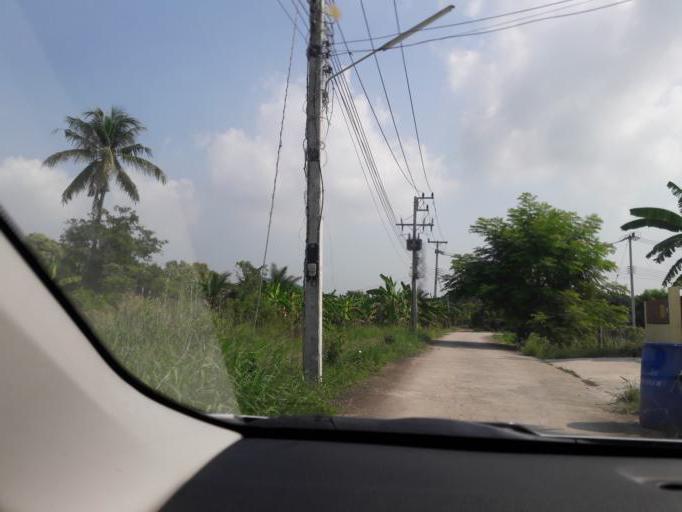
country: TH
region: Ang Thong
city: Ang Thong
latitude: 14.5454
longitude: 100.4405
